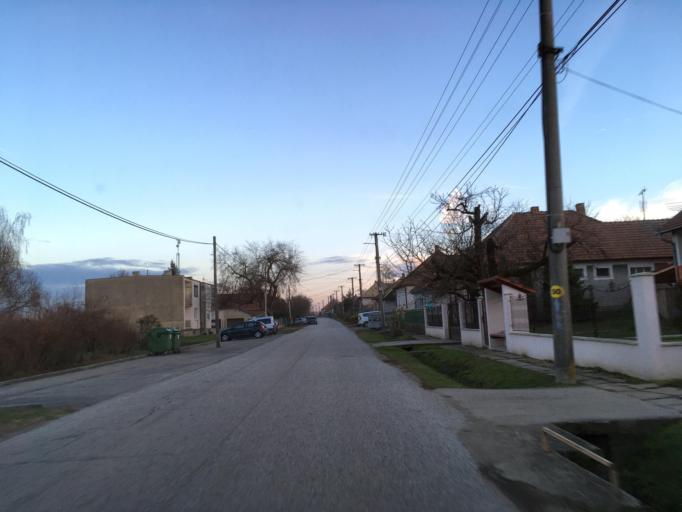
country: SK
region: Nitriansky
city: Svodin
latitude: 47.8688
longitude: 18.4648
